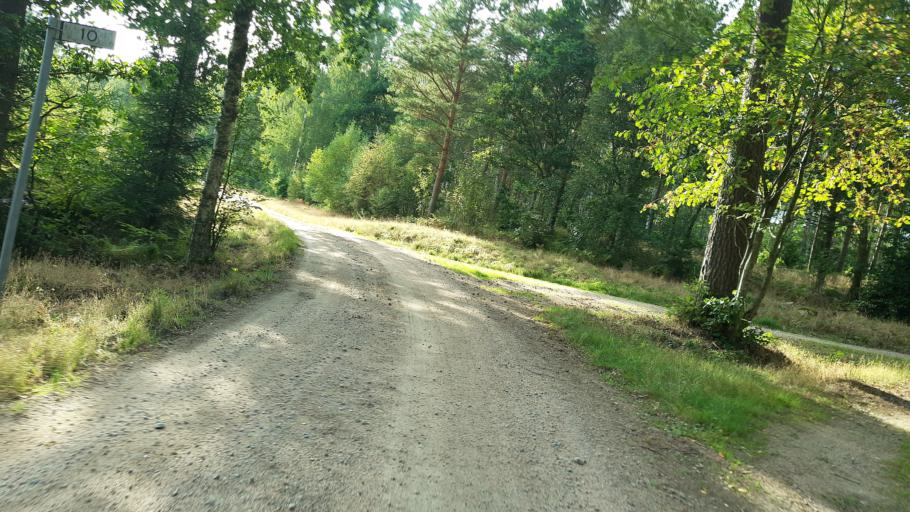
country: SE
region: Blekinge
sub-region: Ronneby Kommun
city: Kallinge
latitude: 56.2385
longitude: 15.3903
